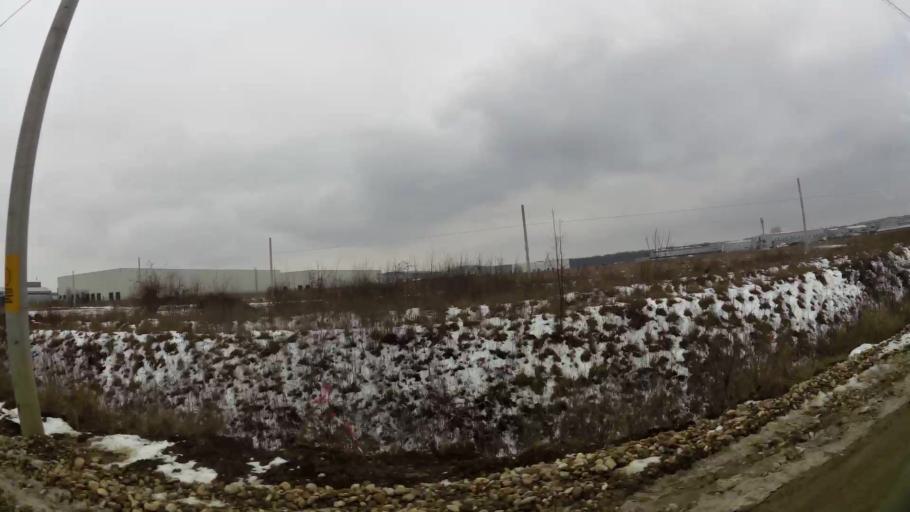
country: RO
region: Ilfov
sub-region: Comuna Otopeni
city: Otopeni
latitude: 44.5456
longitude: 26.0867
